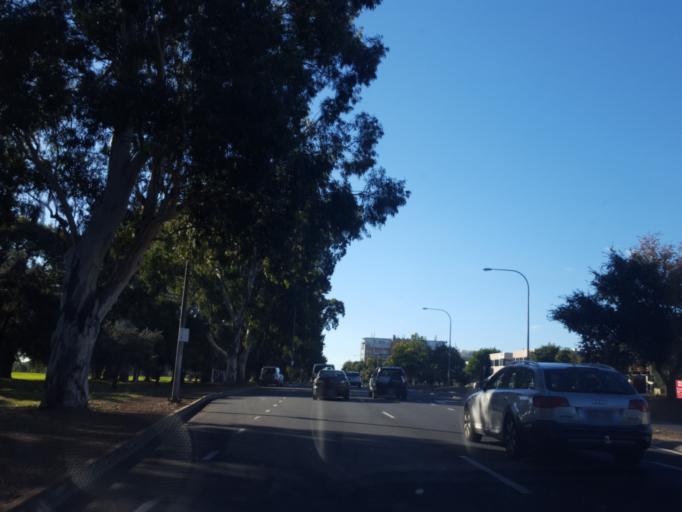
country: AU
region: South Australia
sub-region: Unley
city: Fullarton
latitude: -34.9372
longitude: 138.6241
